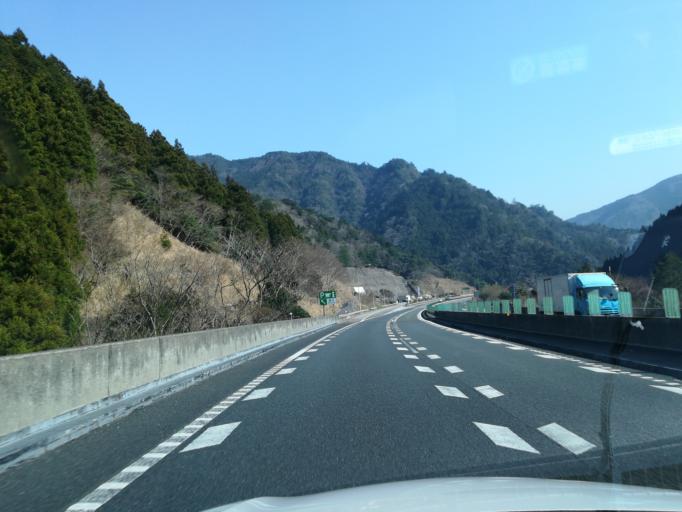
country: JP
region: Ehime
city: Kawanoecho
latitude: 33.9082
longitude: 133.6298
